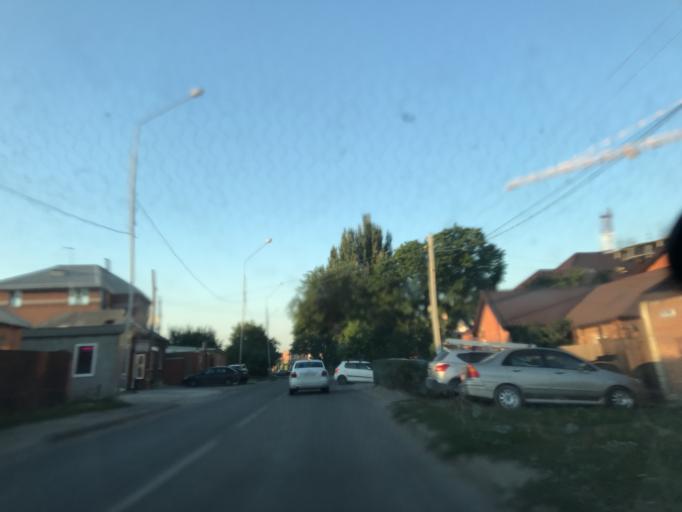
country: RU
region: Rostov
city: Imeni Chkalova
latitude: 47.2398
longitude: 39.7763
